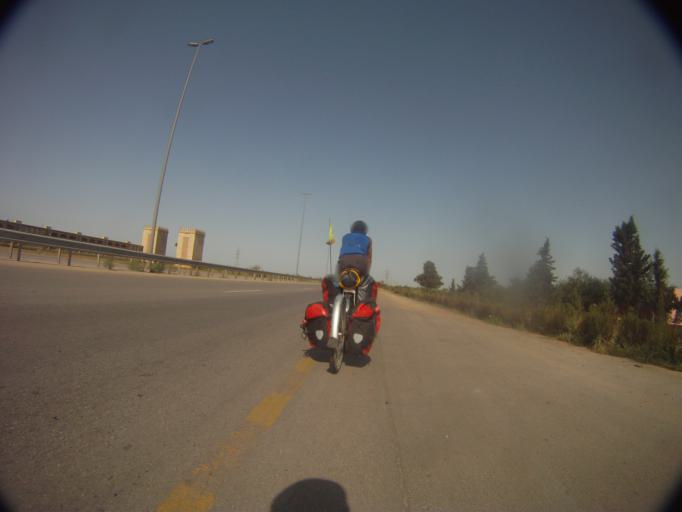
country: AZ
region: Samux
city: Samux
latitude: 40.6886
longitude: 46.4781
